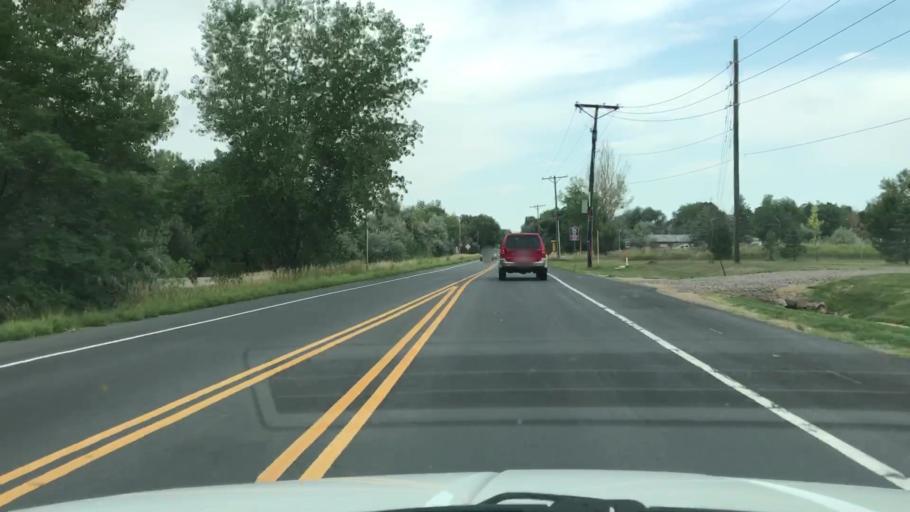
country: US
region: Colorado
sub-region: Boulder County
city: Louisville
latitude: 40.0001
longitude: -105.1727
